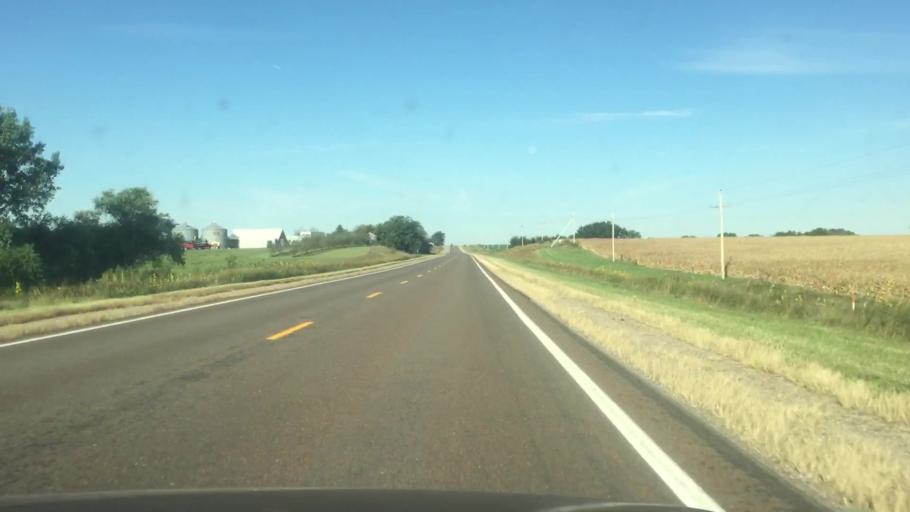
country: US
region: Nebraska
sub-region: Jefferson County
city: Fairbury
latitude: 40.1472
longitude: -97.3556
